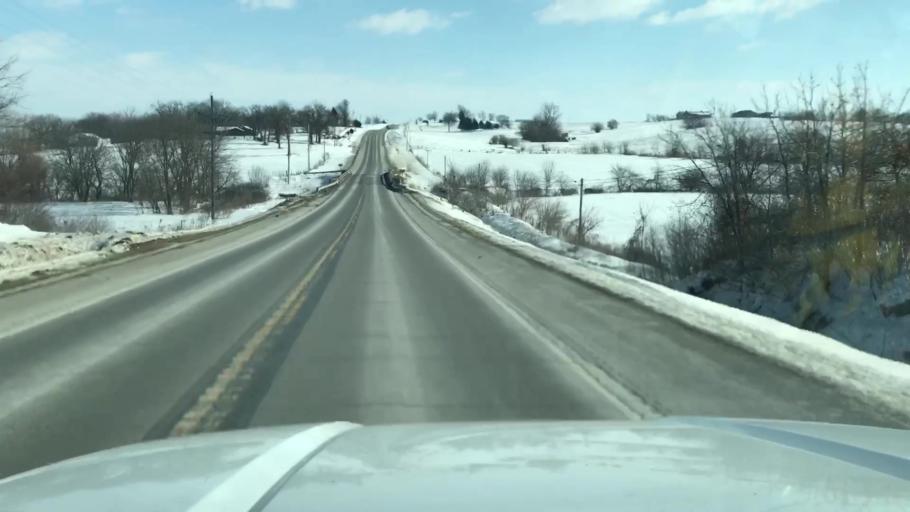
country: US
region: Missouri
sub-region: Nodaway County
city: Maryville
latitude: 40.3445
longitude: -94.7812
